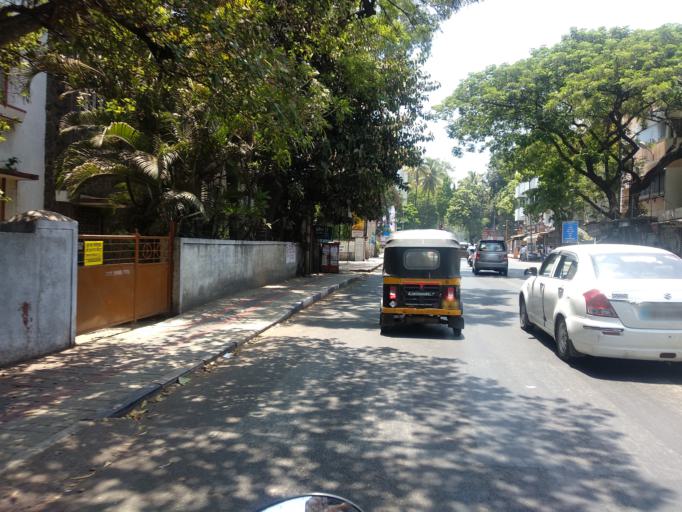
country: IN
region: Maharashtra
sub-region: Pune Division
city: Pune
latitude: 18.5044
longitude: 73.8498
